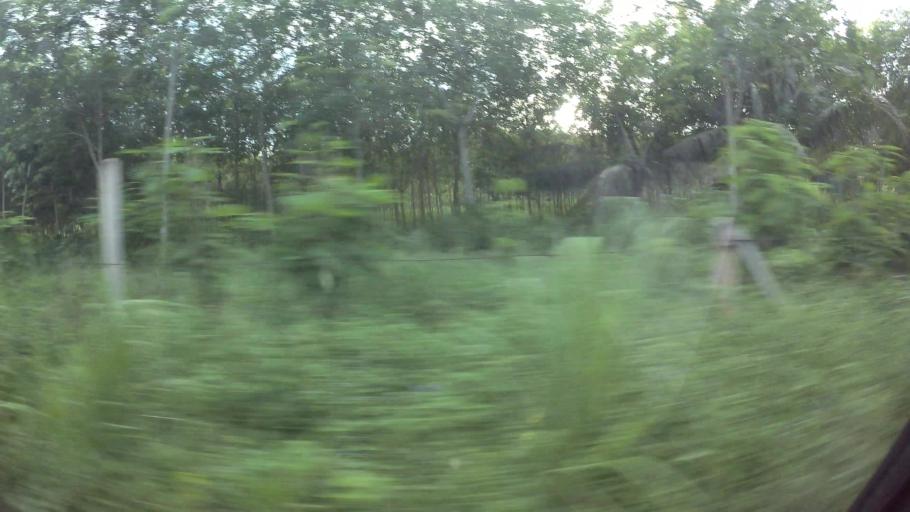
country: TH
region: Chon Buri
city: Sattahip
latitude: 12.6975
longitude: 100.9265
